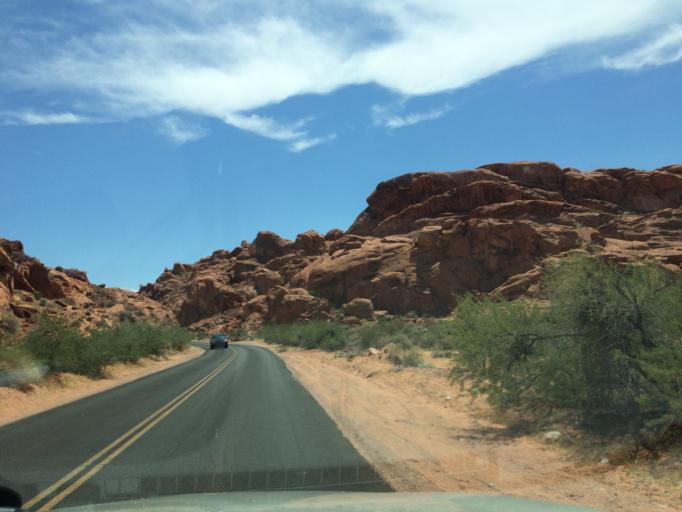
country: US
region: Nevada
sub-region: Clark County
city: Moapa Valley
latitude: 36.4393
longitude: -114.5171
